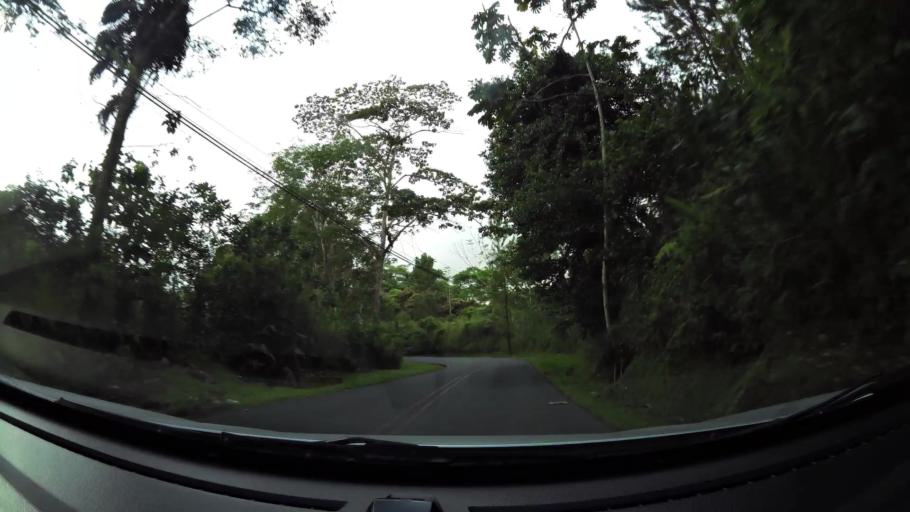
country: CR
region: Cartago
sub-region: Canton de Turrialba
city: La Suiza
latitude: 9.9737
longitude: -83.5703
